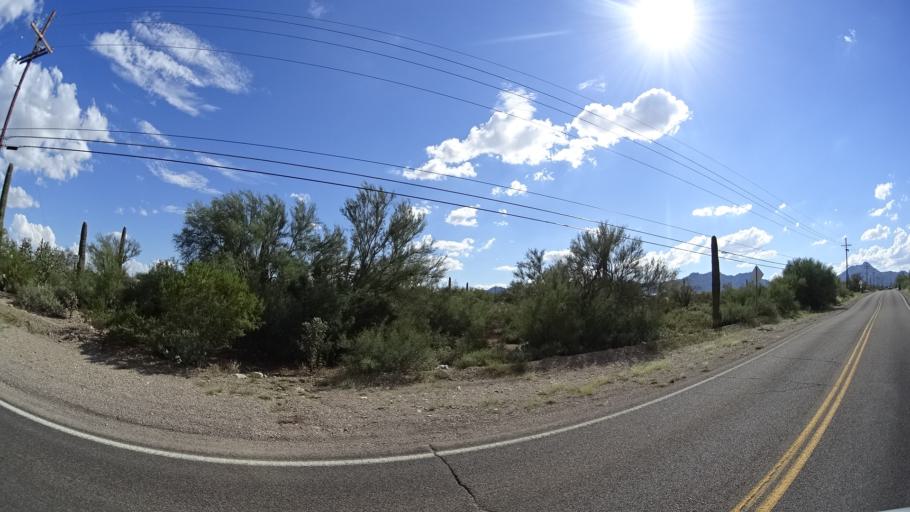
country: US
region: Arizona
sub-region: Pima County
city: Flowing Wells
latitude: 32.2798
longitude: -111.0502
